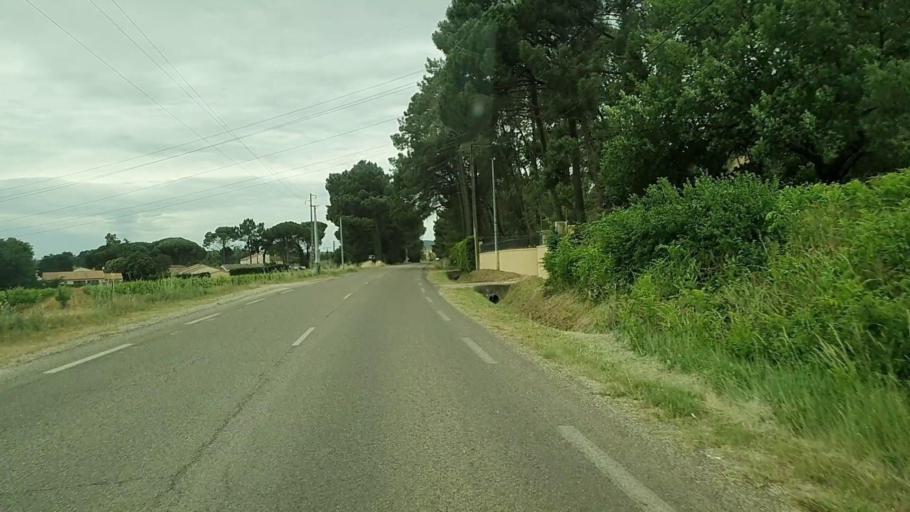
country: FR
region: Languedoc-Roussillon
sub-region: Departement du Gard
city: Tresques
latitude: 44.1207
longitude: 4.5971
